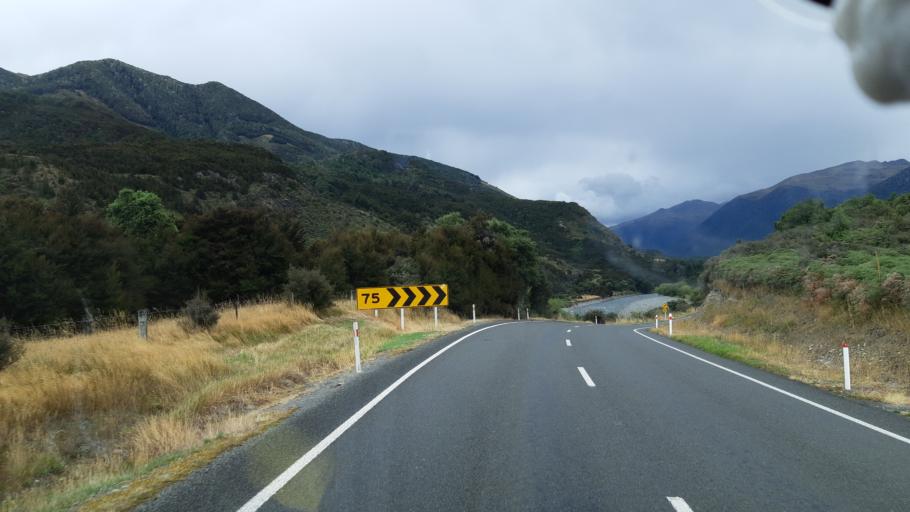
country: NZ
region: Canterbury
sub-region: Hurunui District
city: Amberley
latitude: -42.5703
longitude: 172.3628
